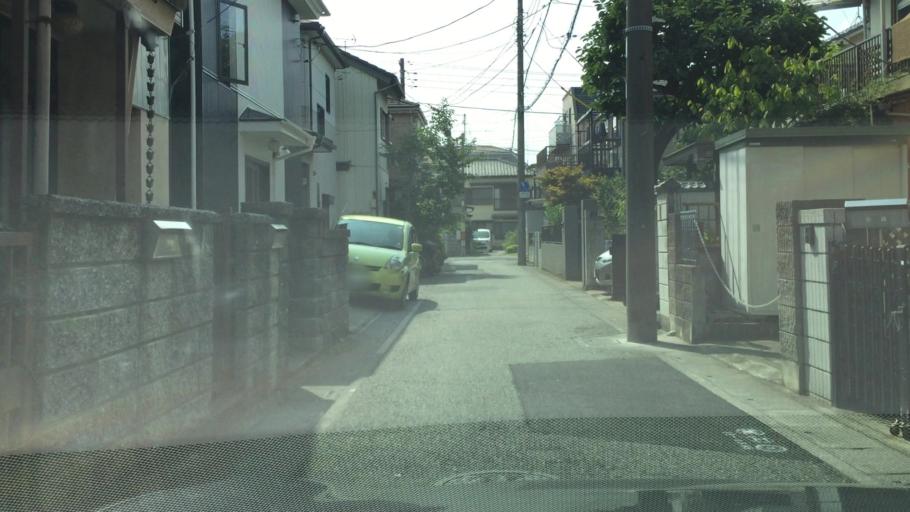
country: JP
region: Saitama
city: Yono
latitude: 35.9219
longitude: 139.6070
